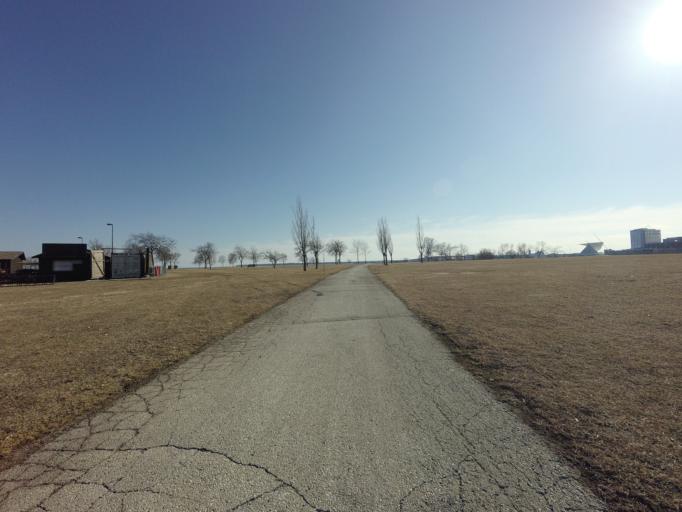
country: US
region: Wisconsin
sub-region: Milwaukee County
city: Milwaukee
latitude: 43.0448
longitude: -87.8905
